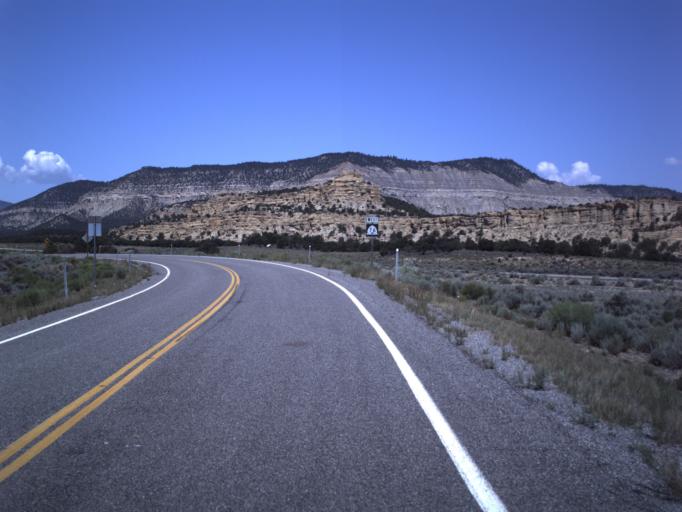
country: US
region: Utah
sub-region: Emery County
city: Ferron
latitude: 38.7555
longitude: -111.3811
